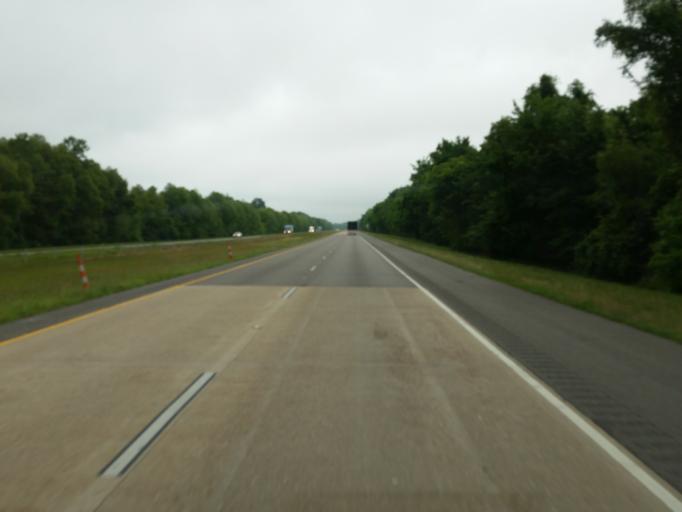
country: US
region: Louisiana
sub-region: Madison Parish
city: Tallulah
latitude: 32.3462
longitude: -91.0823
